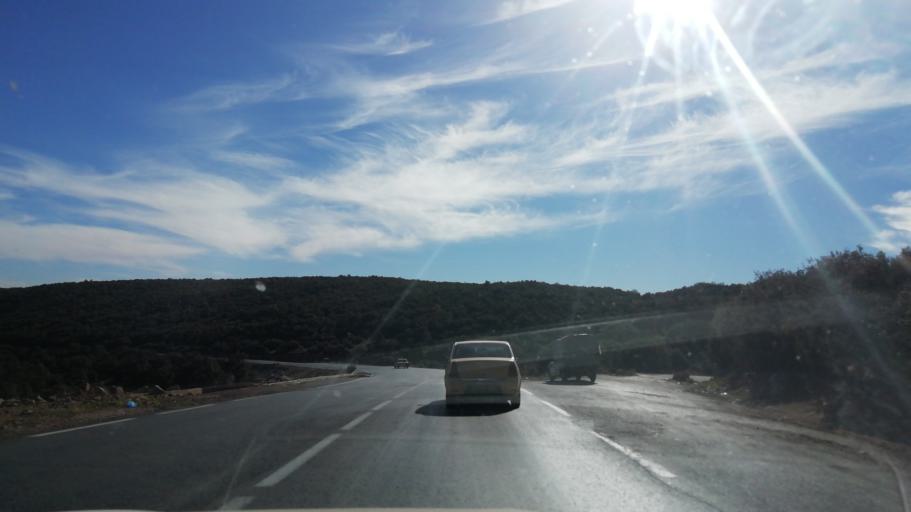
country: DZ
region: Tlemcen
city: Sebdou
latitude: 34.7460
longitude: -1.3498
